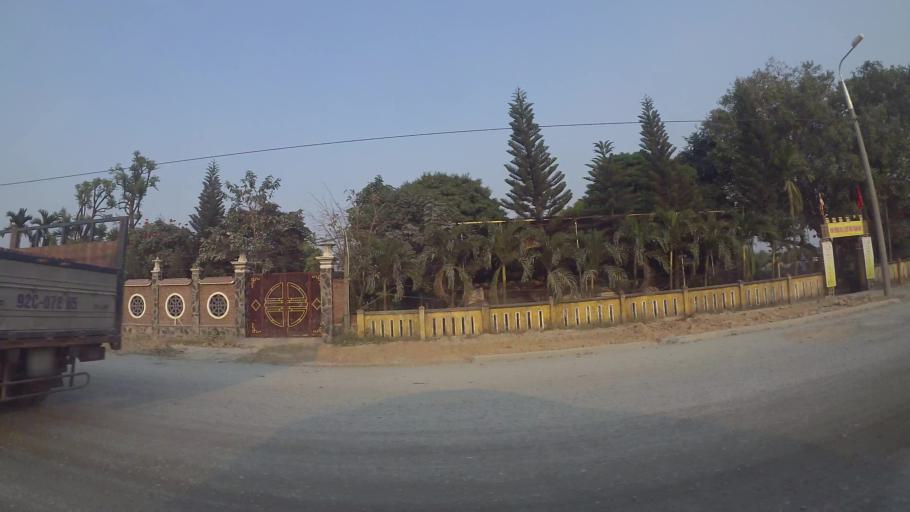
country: VN
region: Da Nang
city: Ngu Hanh Son
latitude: 15.9619
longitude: 108.2311
